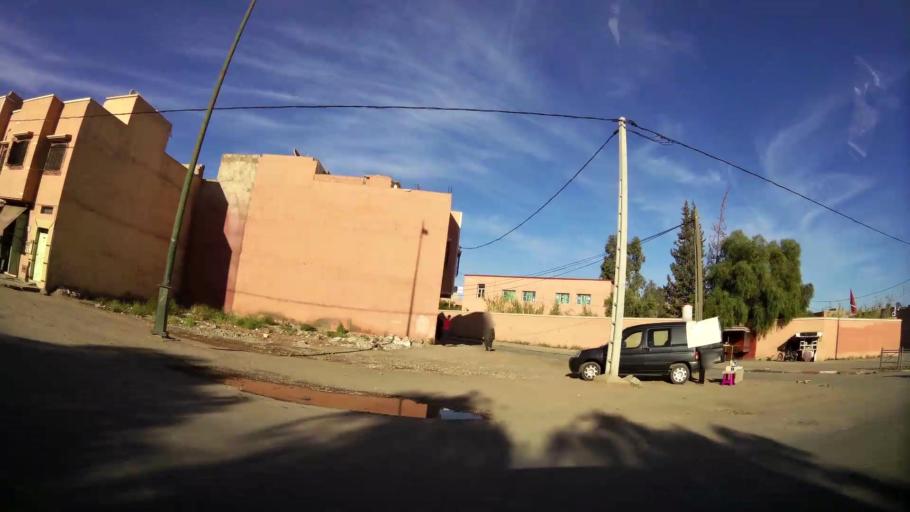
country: MA
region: Marrakech-Tensift-Al Haouz
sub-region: Marrakech
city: Marrakesh
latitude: 31.6791
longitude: -8.0602
